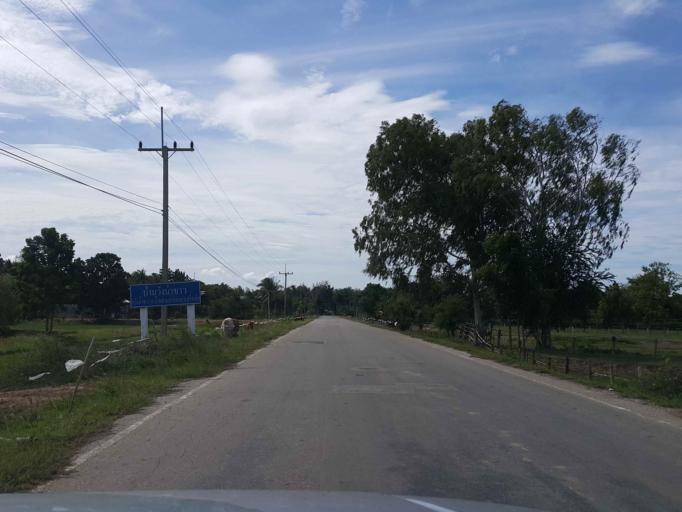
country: TH
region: Sukhothai
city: Ban Dan Lan Hoi
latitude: 17.1199
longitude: 99.5337
